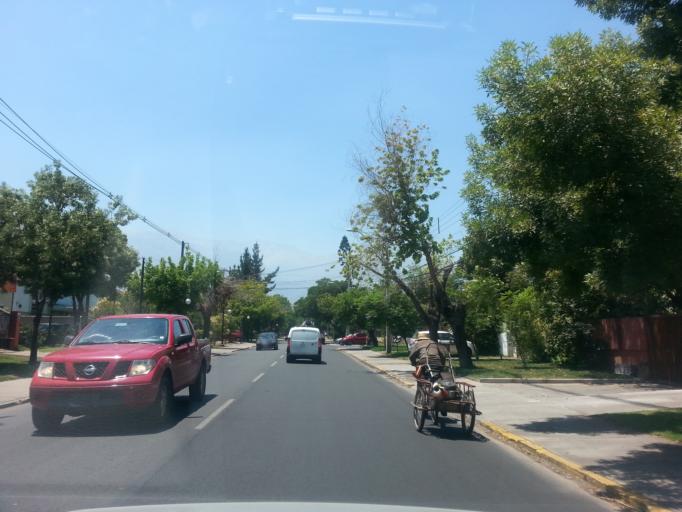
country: CL
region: Santiago Metropolitan
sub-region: Provincia de Santiago
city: Villa Presidente Frei, Nunoa, Santiago, Chile
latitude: -33.4501
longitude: -70.5881
